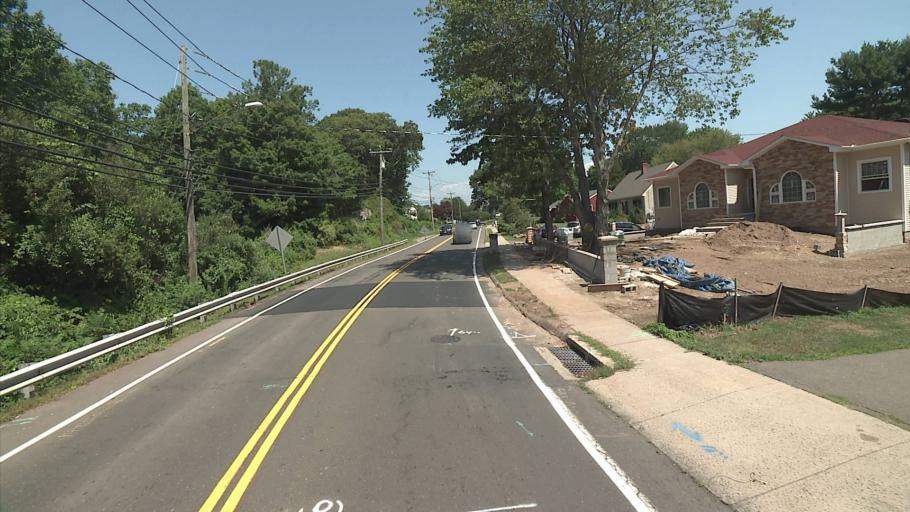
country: US
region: Connecticut
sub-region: New Haven County
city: Branford Center
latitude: 41.2687
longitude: -72.8317
